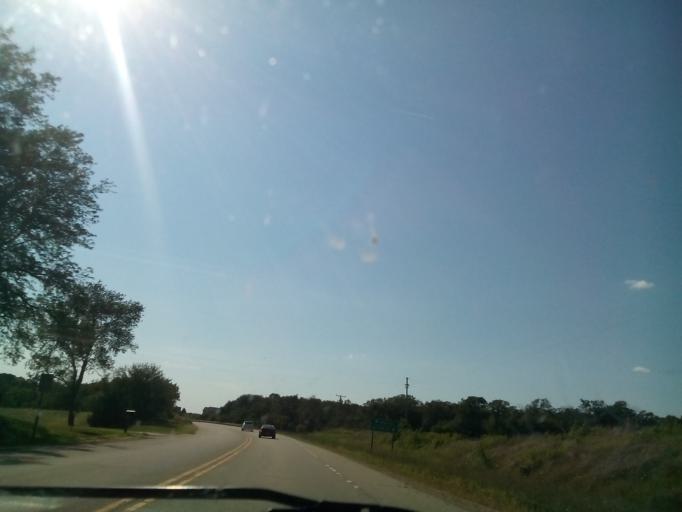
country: US
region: Wisconsin
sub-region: Dane County
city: Belleville
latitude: 42.8661
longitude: -89.6001
